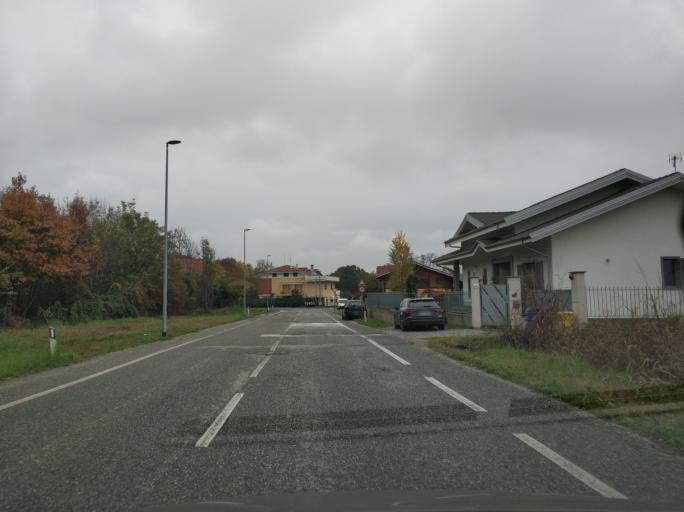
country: IT
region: Piedmont
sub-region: Provincia di Torino
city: Villanova Canavese
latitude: 45.2403
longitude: 7.5547
